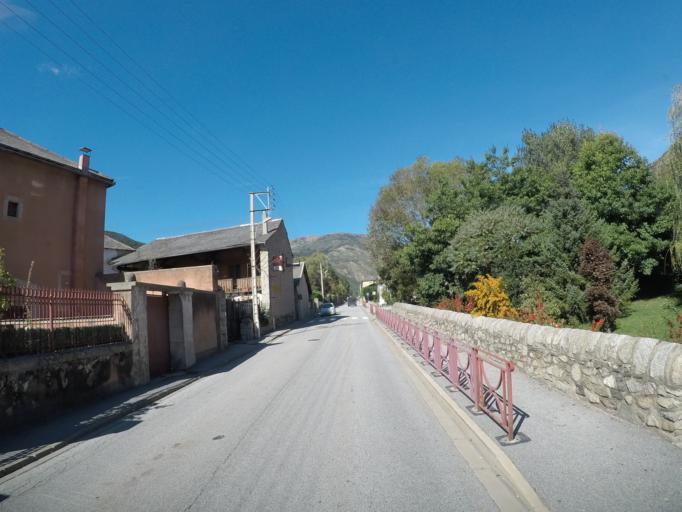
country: ES
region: Catalonia
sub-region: Provincia de Girona
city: Guils de Cerdanya
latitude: 42.4654
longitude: 1.8897
